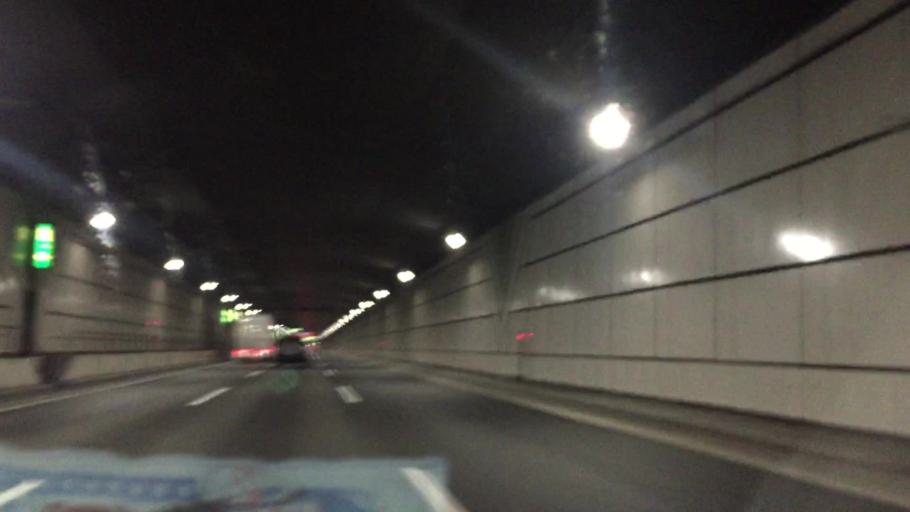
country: JP
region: Kanagawa
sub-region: Kawasaki-shi
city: Kawasaki
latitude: 35.5080
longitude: 139.7774
